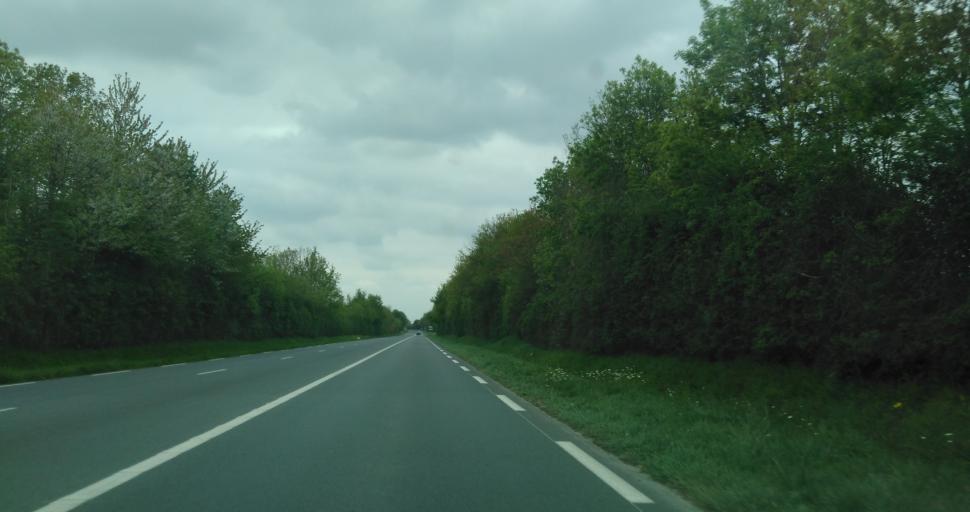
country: FR
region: Poitou-Charentes
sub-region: Departement des Deux-Sevres
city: Champdeniers-Saint-Denis
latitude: 46.4524
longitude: -0.3832
